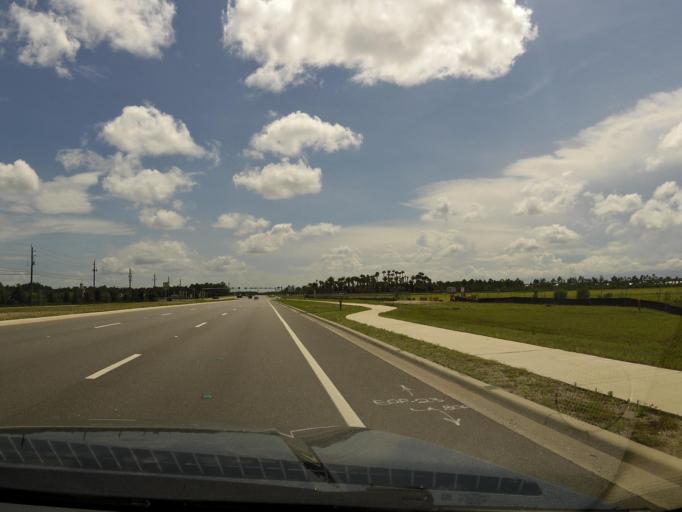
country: US
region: Florida
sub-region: Saint Johns County
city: Palm Valley
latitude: 30.0863
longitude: -81.4701
